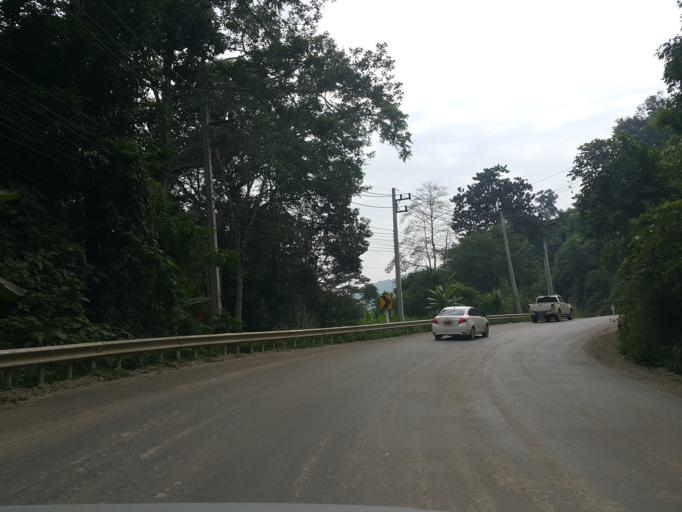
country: TH
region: Chiang Mai
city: Mae Taeng
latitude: 19.1756
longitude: 98.6926
